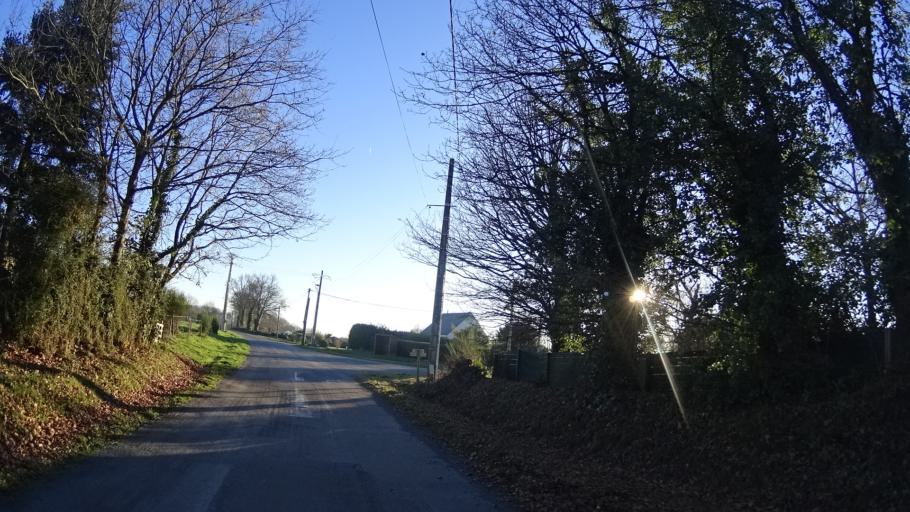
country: FR
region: Brittany
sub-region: Departement du Morbihan
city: Saint-Jean-la-Poterie
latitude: 47.6450
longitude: -2.1324
